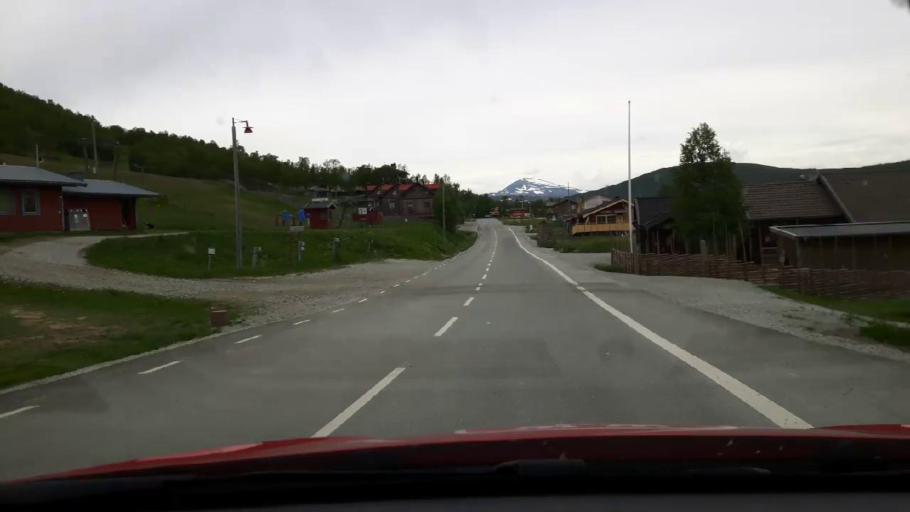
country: NO
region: Sor-Trondelag
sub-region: Tydal
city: Aas
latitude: 62.7015
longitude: 12.3883
